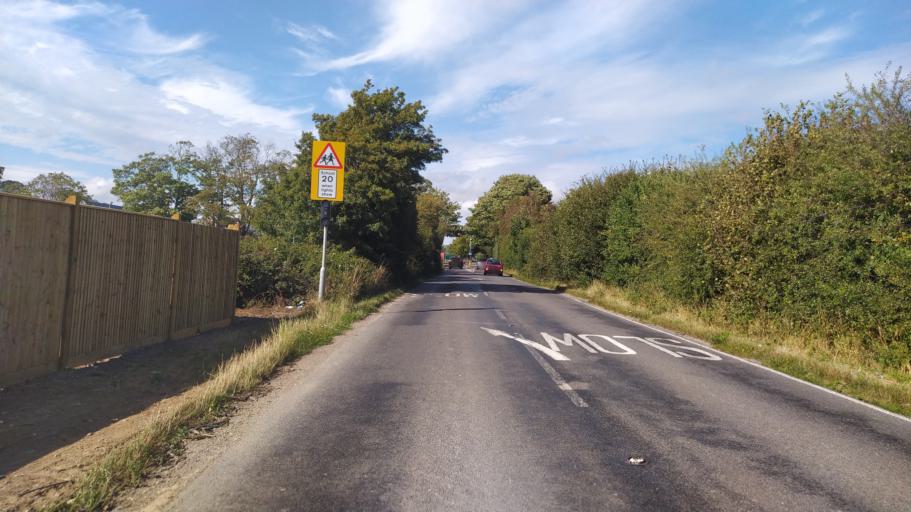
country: GB
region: England
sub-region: West Sussex
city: Chichester
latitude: 50.8205
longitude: -0.7687
